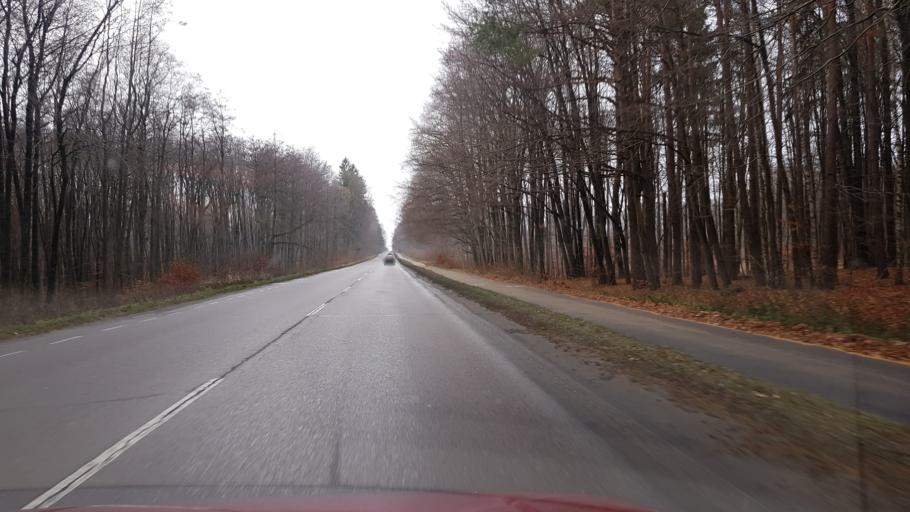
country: PL
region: West Pomeranian Voivodeship
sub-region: Koszalin
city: Koszalin
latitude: 54.2151
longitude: 16.1309
